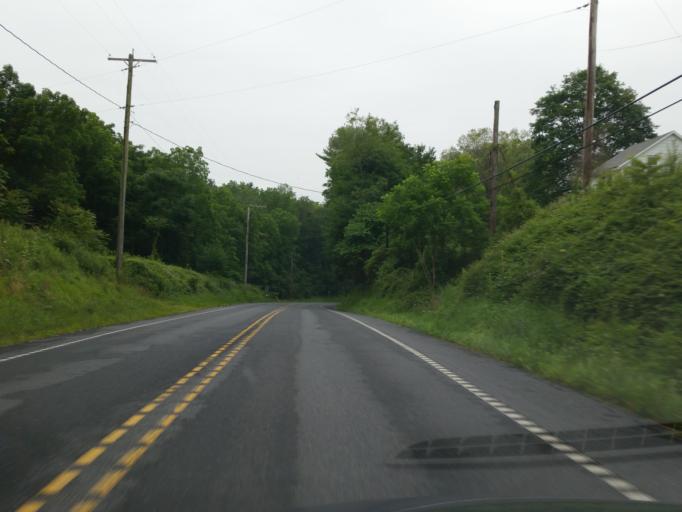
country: US
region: Pennsylvania
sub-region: Schuylkill County
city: Tower City
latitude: 40.5084
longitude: -76.5208
